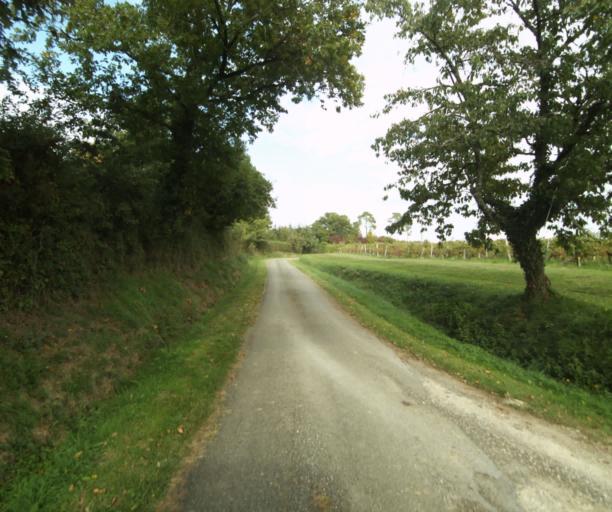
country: FR
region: Midi-Pyrenees
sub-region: Departement du Gers
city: Eauze
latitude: 43.9054
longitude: 0.0915
